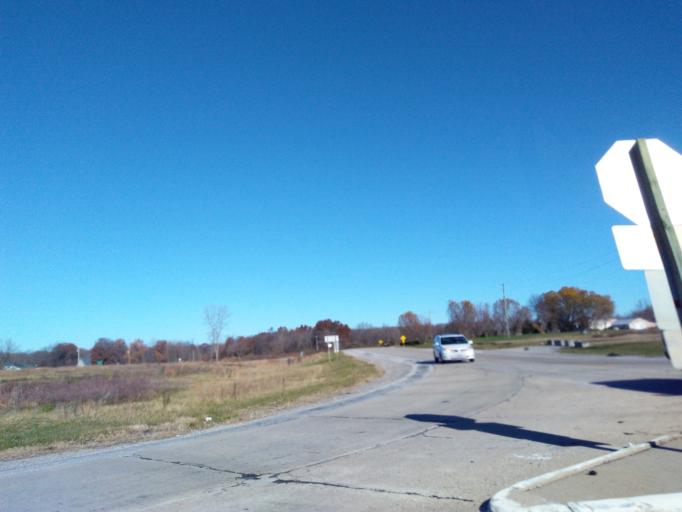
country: US
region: Illinois
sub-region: Madison County
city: Saint Jacob
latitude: 38.7161
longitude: -89.8000
